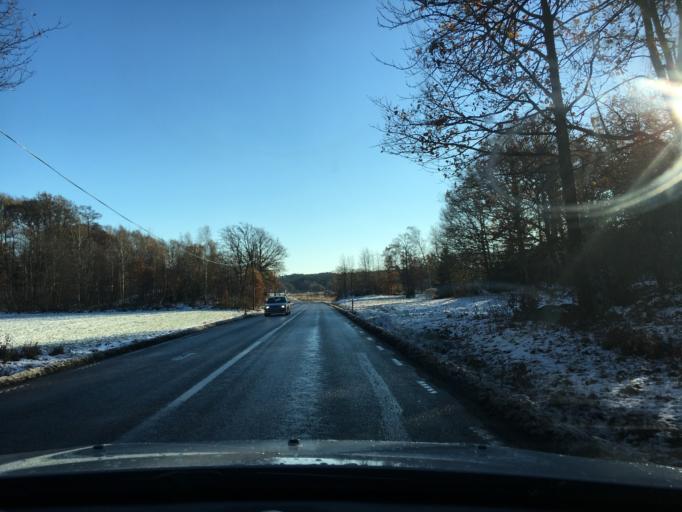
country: SE
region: Vaestra Goetaland
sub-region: Tjorns Kommun
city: Myggenas
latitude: 58.1082
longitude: 11.7002
